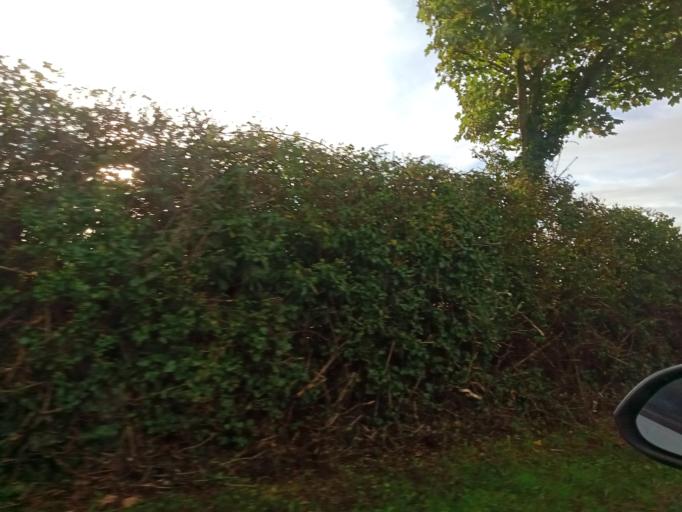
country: IE
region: Leinster
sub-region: Laois
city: Stradbally
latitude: 53.0045
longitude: -7.2122
